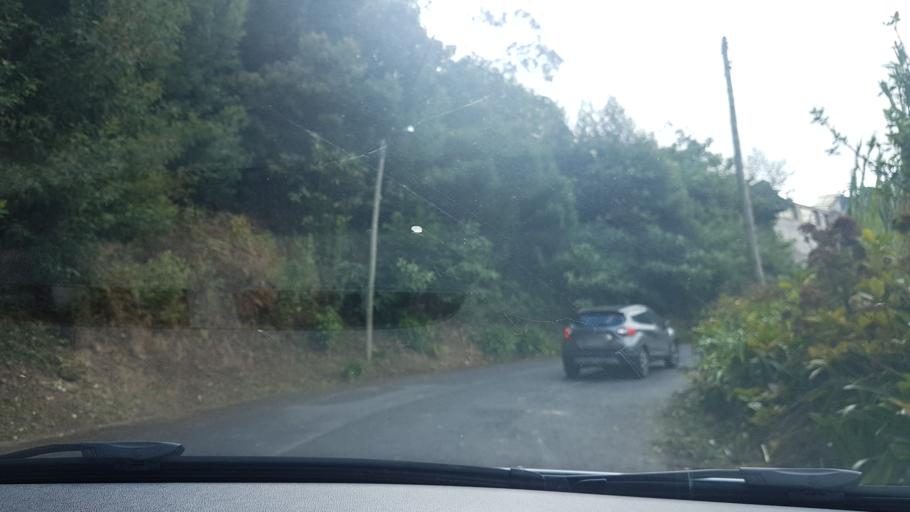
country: PT
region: Madeira
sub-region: Sao Vicente
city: Sao Vicente
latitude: 32.7773
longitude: -17.0284
